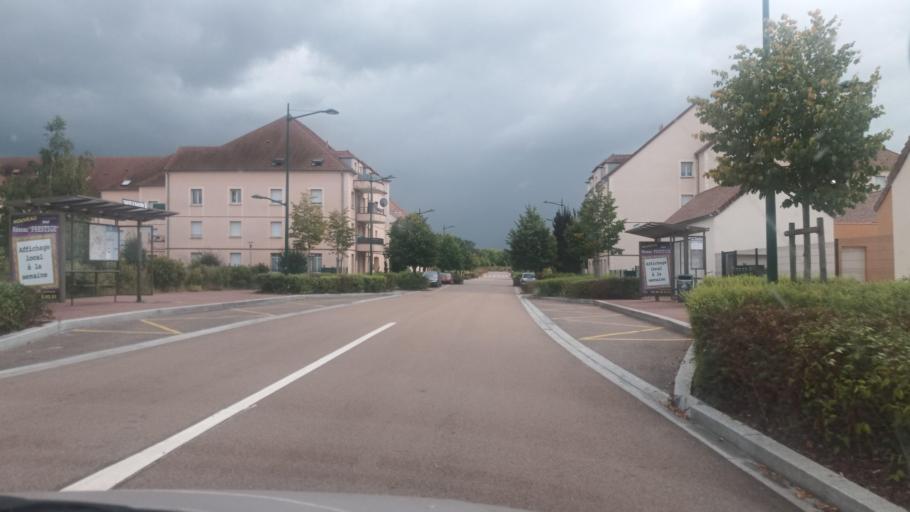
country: FR
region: Bourgogne
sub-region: Departement de l'Yonne
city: Paron
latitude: 48.1870
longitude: 3.2471
